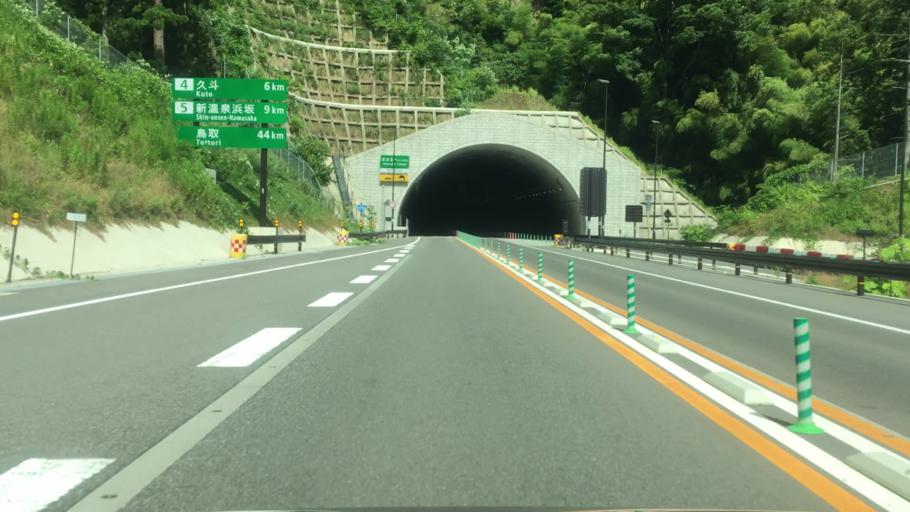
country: JP
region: Hyogo
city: Toyooka
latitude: 35.6393
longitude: 134.5635
